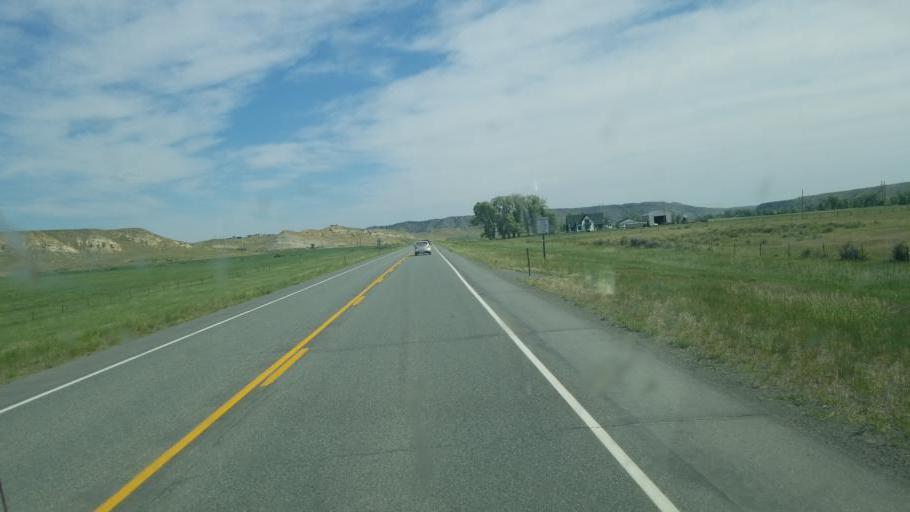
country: US
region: Wyoming
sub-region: Park County
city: Cody
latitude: 44.1640
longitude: -108.8761
